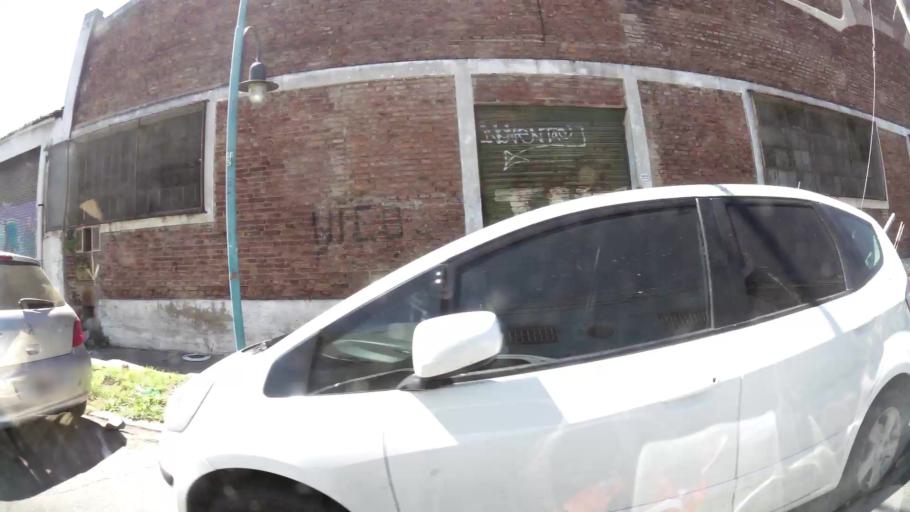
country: AR
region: Buenos Aires
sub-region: Partido de General San Martin
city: General San Martin
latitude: -34.5353
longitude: -58.5435
